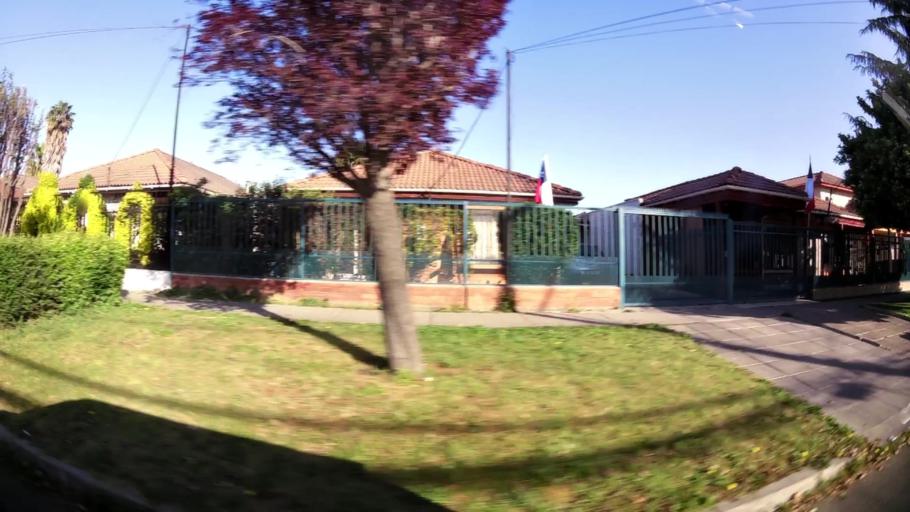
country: CL
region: Santiago Metropolitan
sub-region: Provincia de Santiago
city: Lo Prado
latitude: -33.4855
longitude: -70.7564
